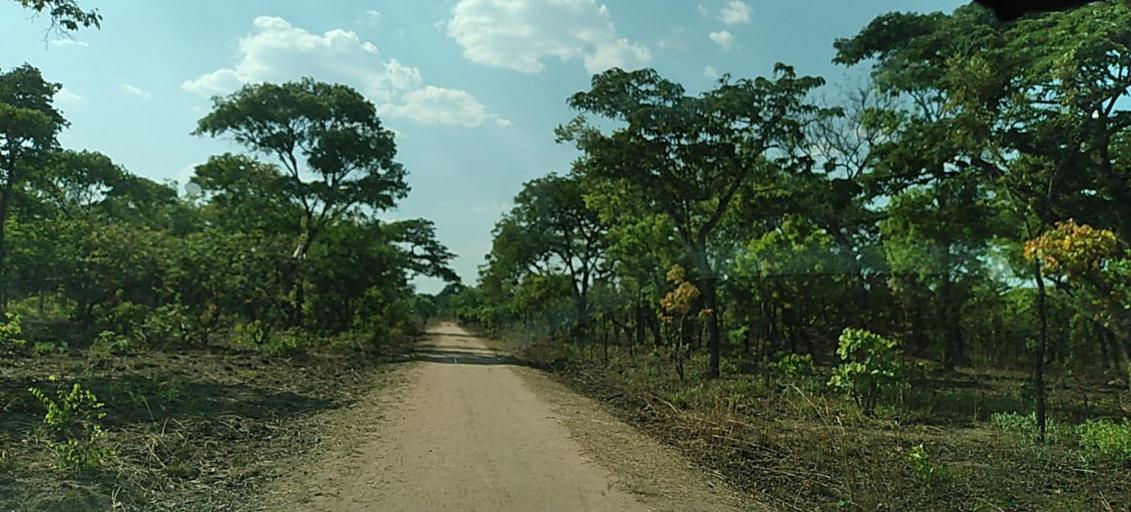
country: ZM
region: North-Western
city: Kalengwa
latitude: -13.1021
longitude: 24.9869
